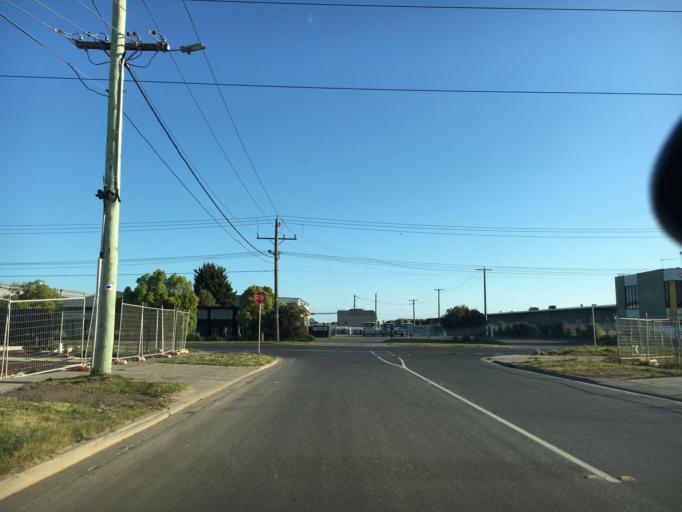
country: AU
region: Victoria
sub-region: Kingston
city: Clayton South
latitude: -37.9412
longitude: 145.1263
